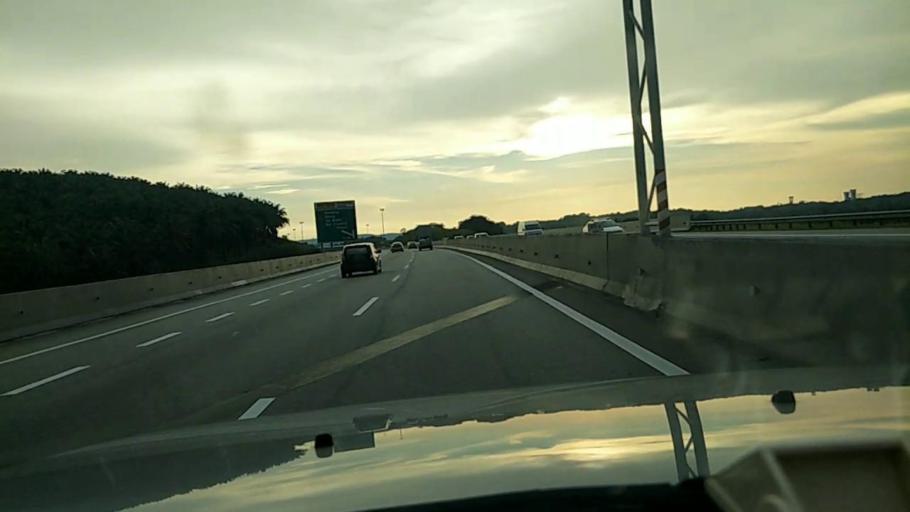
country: MY
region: Selangor
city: Kuang
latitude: 3.2715
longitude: 101.5389
